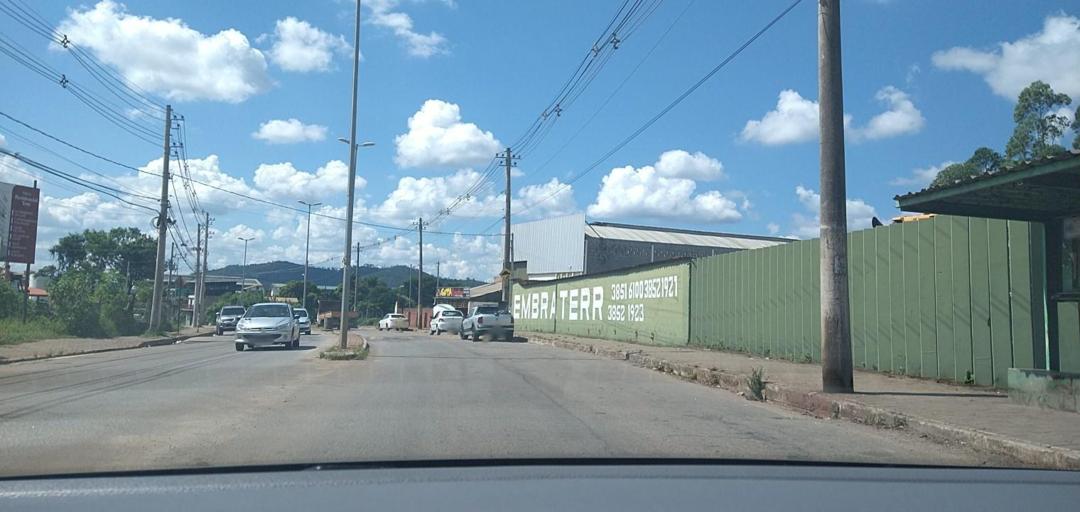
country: BR
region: Minas Gerais
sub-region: Joao Monlevade
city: Joao Monlevade
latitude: -19.8301
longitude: -43.1878
